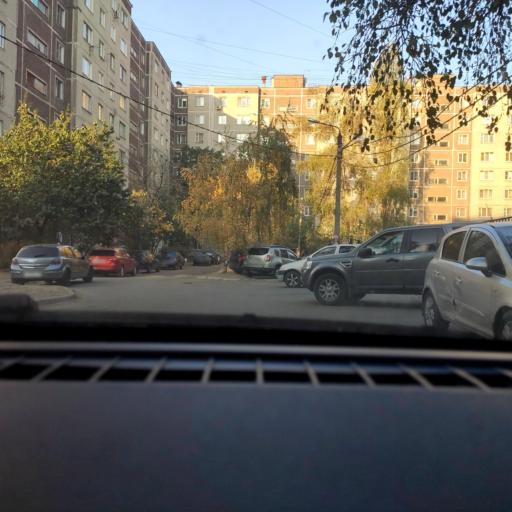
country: RU
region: Voronezj
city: Maslovka
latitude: 51.5955
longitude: 39.2389
